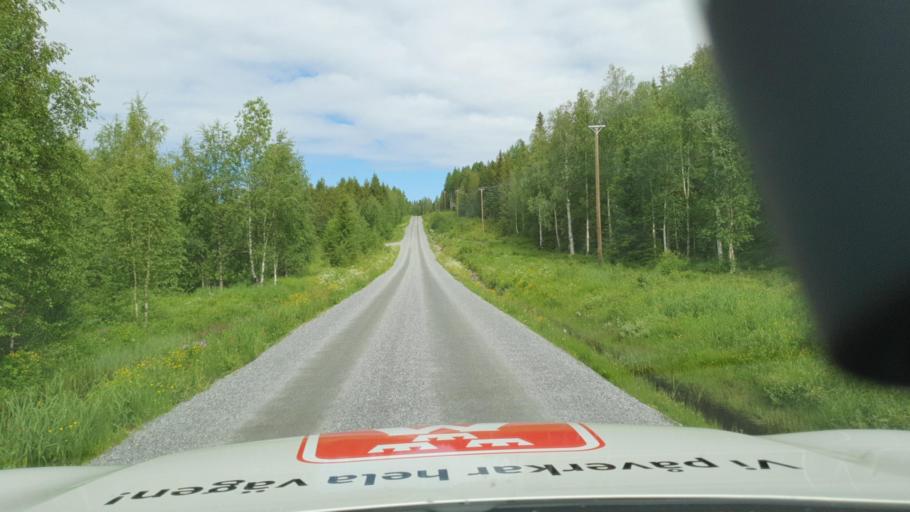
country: SE
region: Vaesterbotten
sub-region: Skelleftea Kommun
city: Langsele
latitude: 64.6123
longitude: 20.2715
